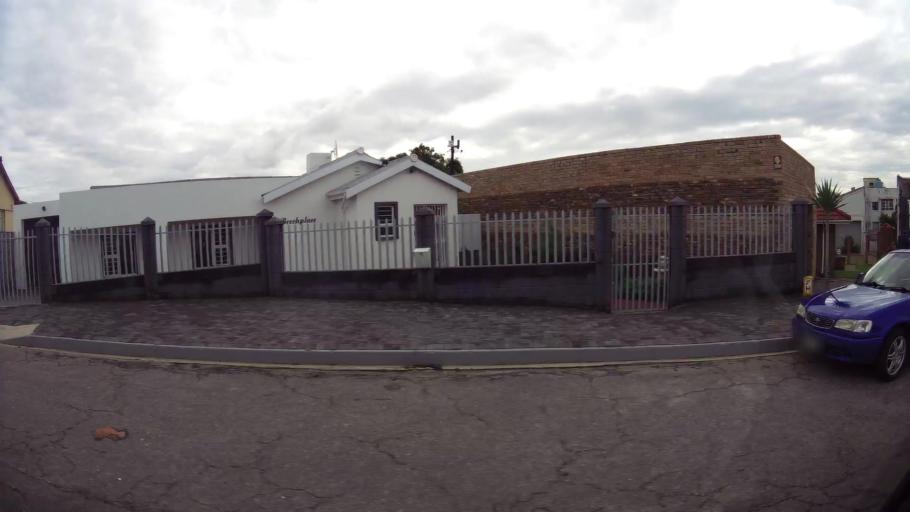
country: ZA
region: Eastern Cape
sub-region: Nelson Mandela Bay Metropolitan Municipality
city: Port Elizabeth
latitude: -33.9390
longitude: 25.5871
